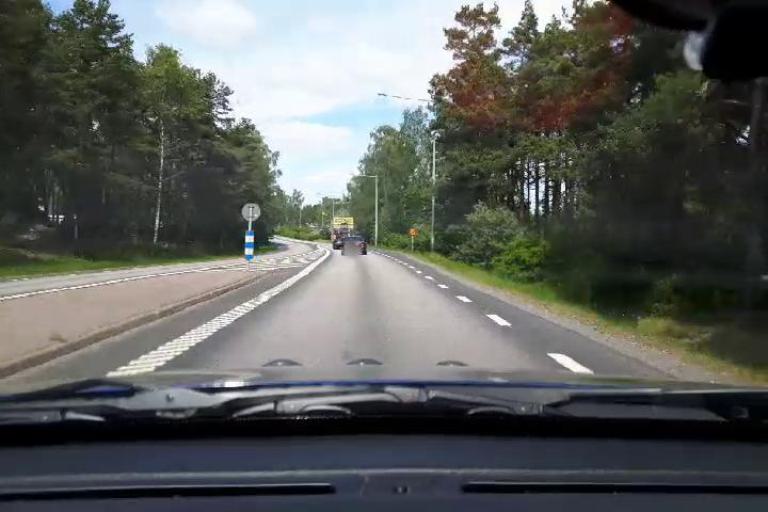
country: SE
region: Uppsala
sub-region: Osthammars Kommun
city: Bjorklinge
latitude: 60.0329
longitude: 17.5523
